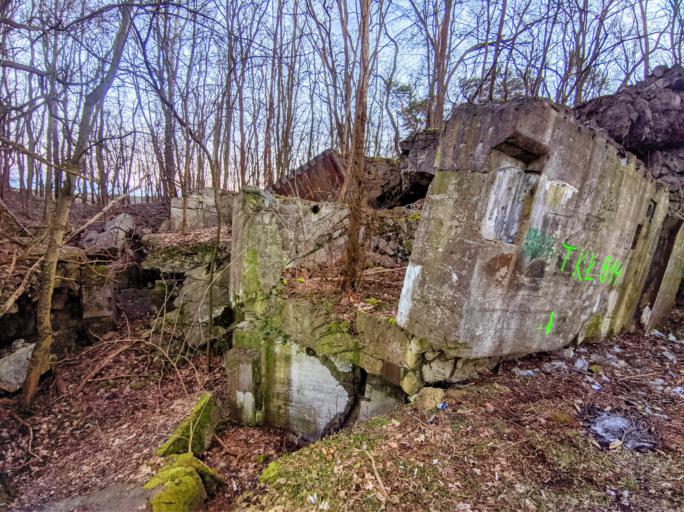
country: PL
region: Lubusz
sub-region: Powiat miedzyrzecki
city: Bledzew
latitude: 52.4897
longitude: 15.4235
